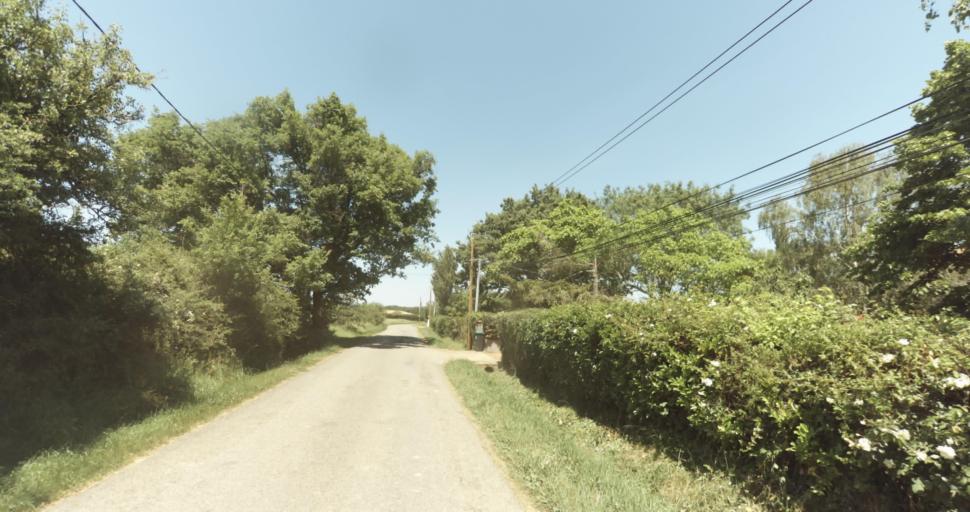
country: FR
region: Midi-Pyrenees
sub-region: Departement de la Haute-Garonne
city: Levignac
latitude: 43.6364
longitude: 1.1878
